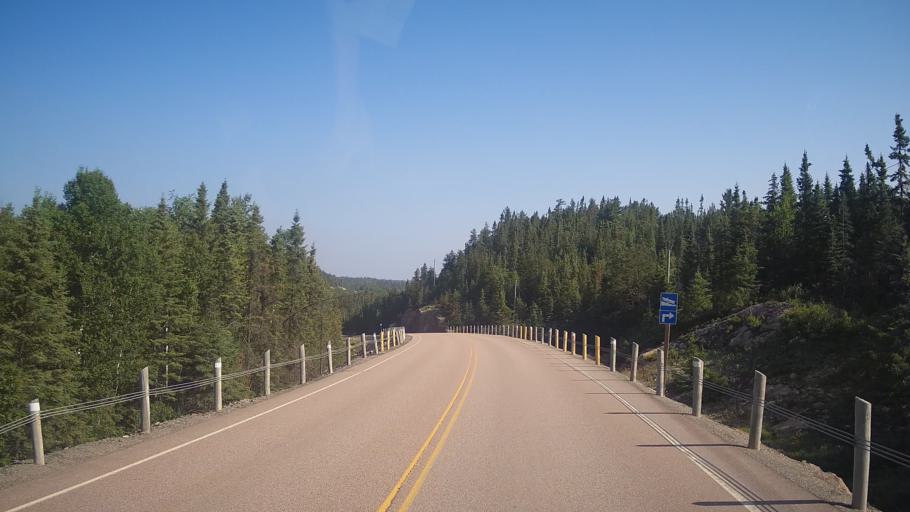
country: CA
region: Ontario
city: Rayside-Balfour
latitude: 47.0123
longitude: -81.6339
